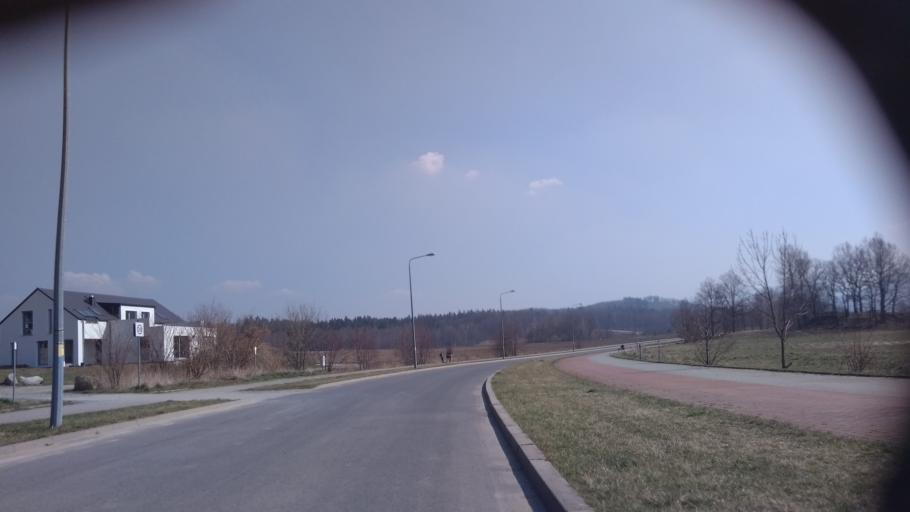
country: PL
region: Lower Silesian Voivodeship
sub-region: Jelenia Gora
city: Cieplice Slaskie Zdroj
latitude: 50.8519
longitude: 15.7004
